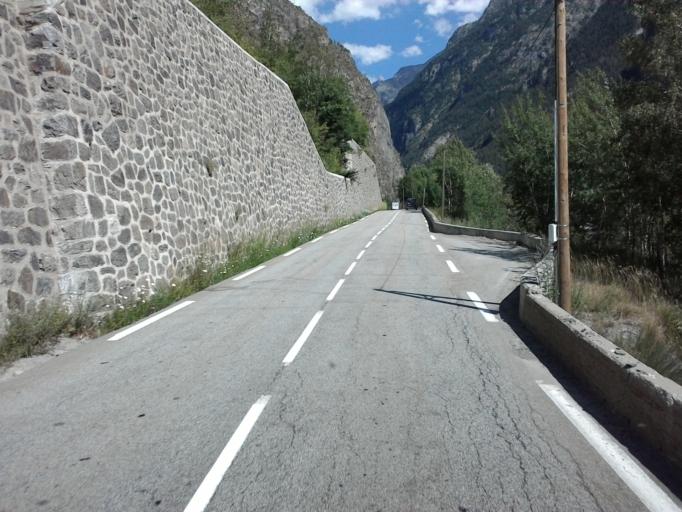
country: FR
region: Rhone-Alpes
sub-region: Departement de l'Isere
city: Mont-de-Lans
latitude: 45.0435
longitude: 6.1642
